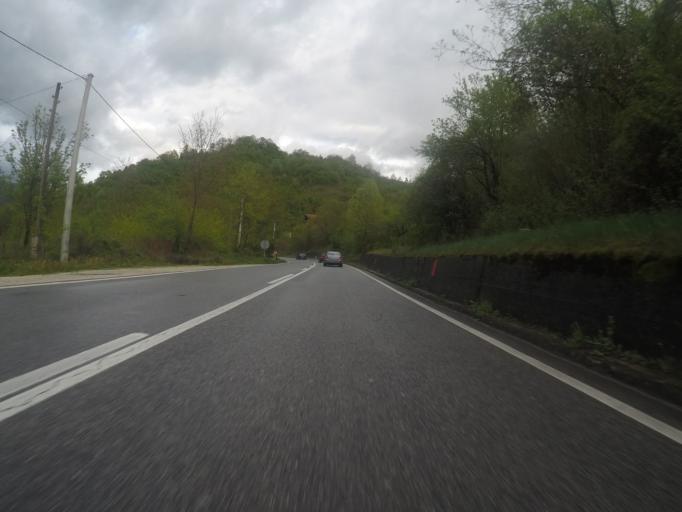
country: BA
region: Federation of Bosnia and Herzegovina
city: Jablanica
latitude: 43.6912
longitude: 17.8392
